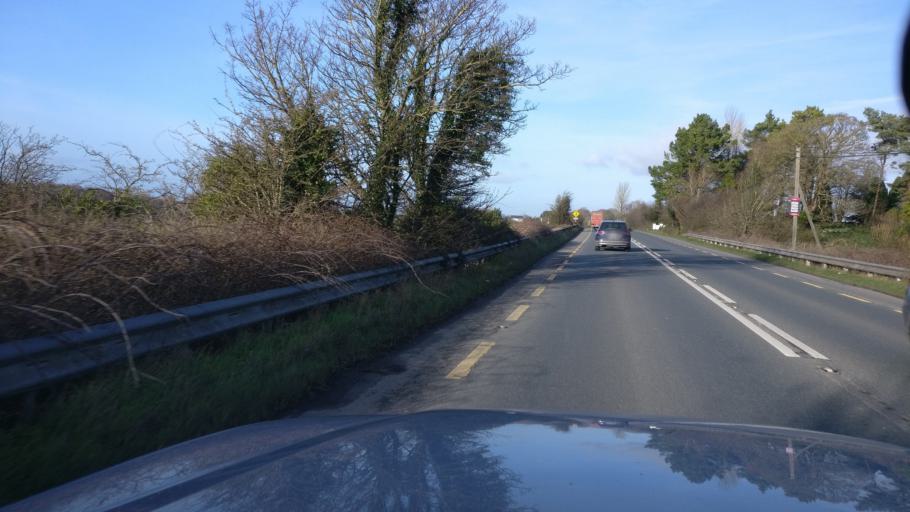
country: IE
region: Leinster
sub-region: Uibh Fhaili
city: Tullamore
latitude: 53.2443
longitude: -7.4777
